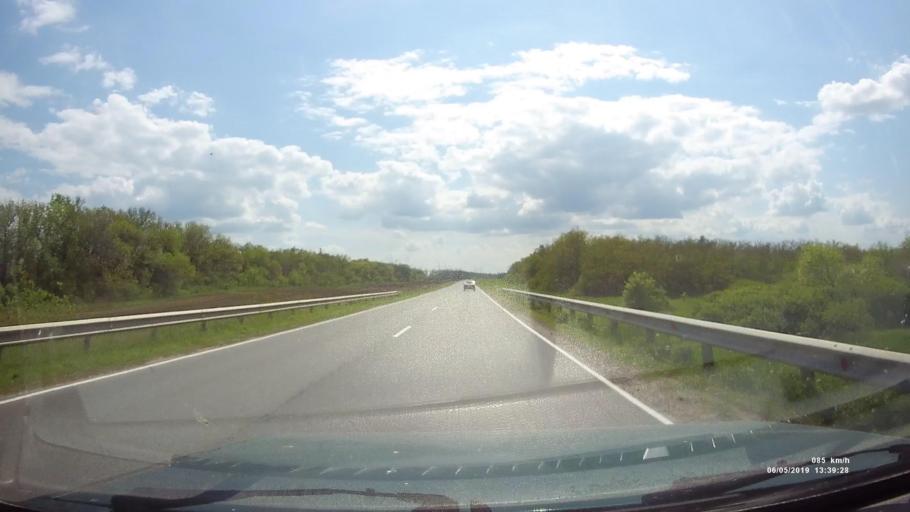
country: RU
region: Rostov
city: Ust'-Donetskiy
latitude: 47.6751
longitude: 40.7026
